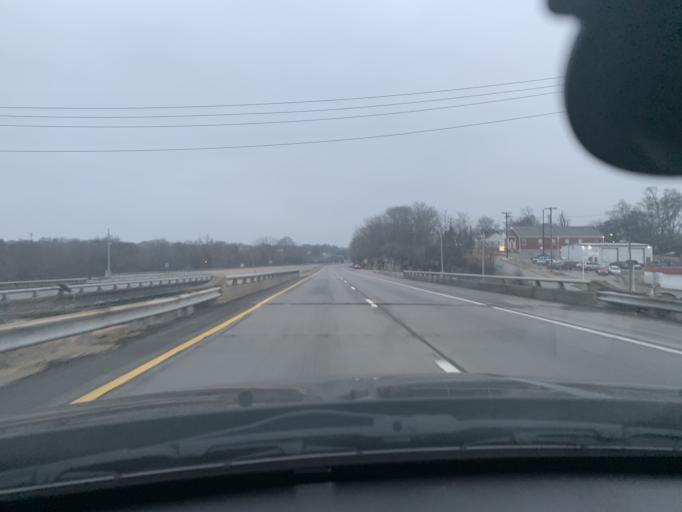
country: US
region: Tennessee
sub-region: Davidson County
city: Nashville
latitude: 36.1938
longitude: -86.7528
